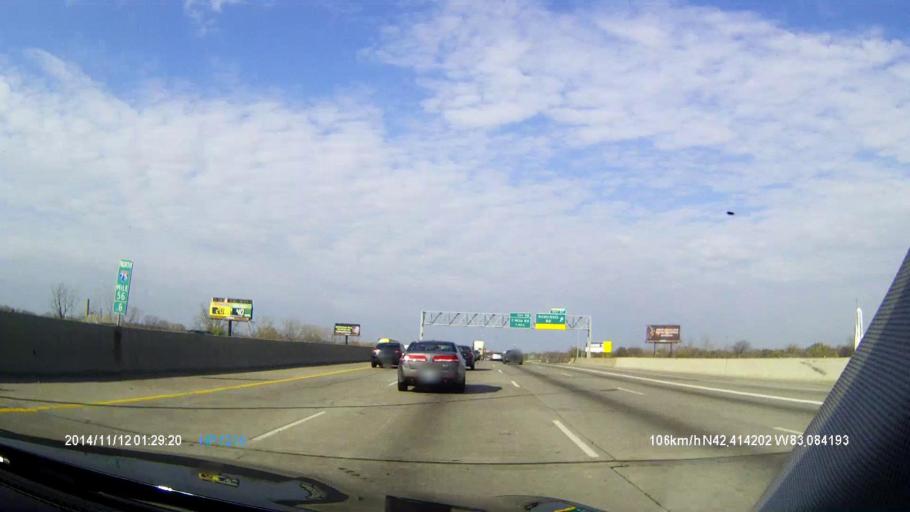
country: US
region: Michigan
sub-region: Wayne County
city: Highland Park
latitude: 42.4142
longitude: -83.0842
